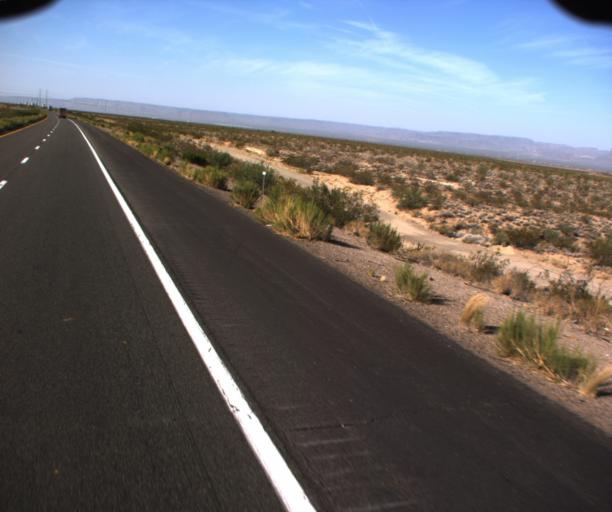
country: US
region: Arizona
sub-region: Mohave County
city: Kingman
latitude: 35.1161
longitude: -114.1143
